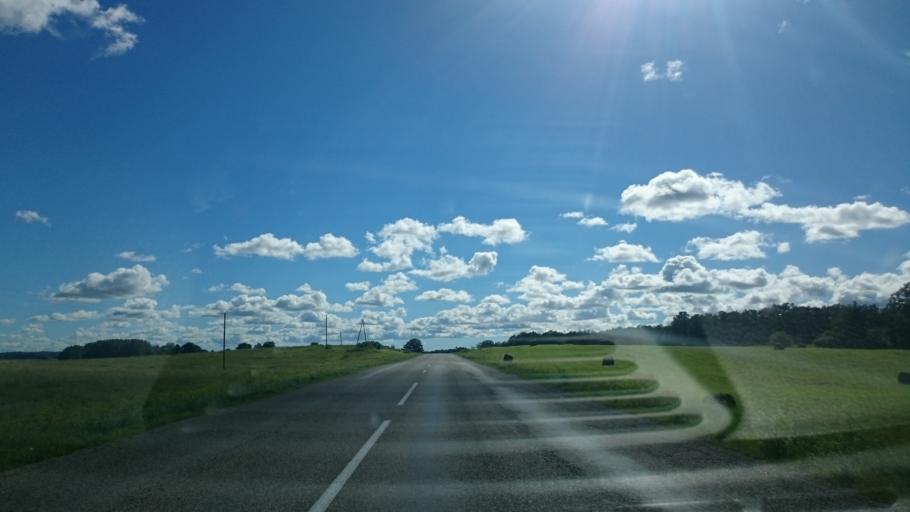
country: LV
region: Aizpute
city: Aizpute
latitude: 56.7729
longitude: 21.6294
